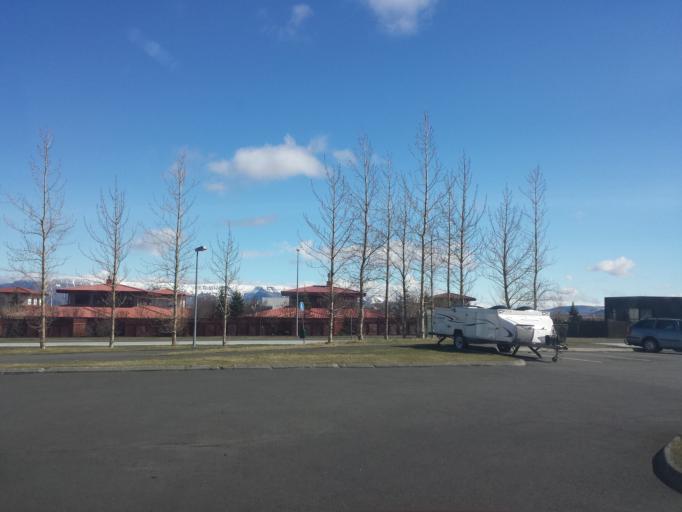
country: IS
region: Capital Region
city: Reykjavik
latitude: 64.0918
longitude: -21.8472
